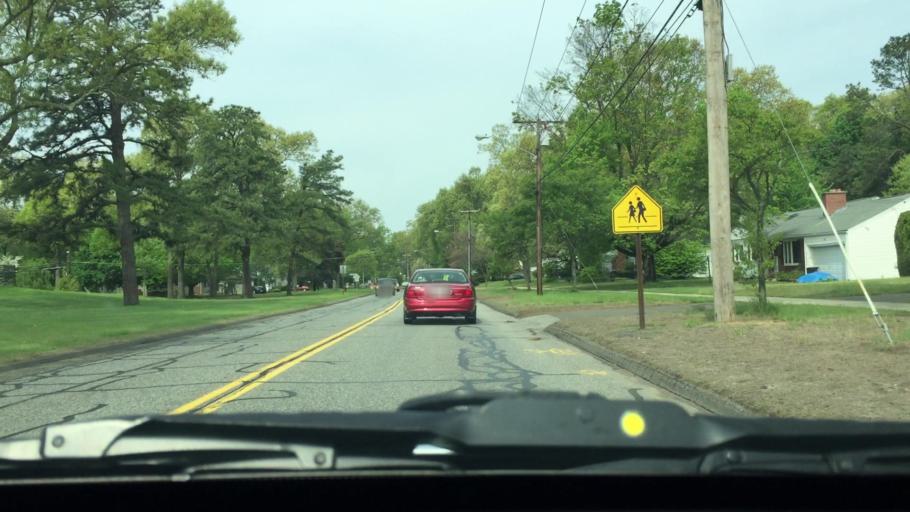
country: US
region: Massachusetts
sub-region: Hampden County
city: Longmeadow
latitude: 42.0574
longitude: -72.5617
